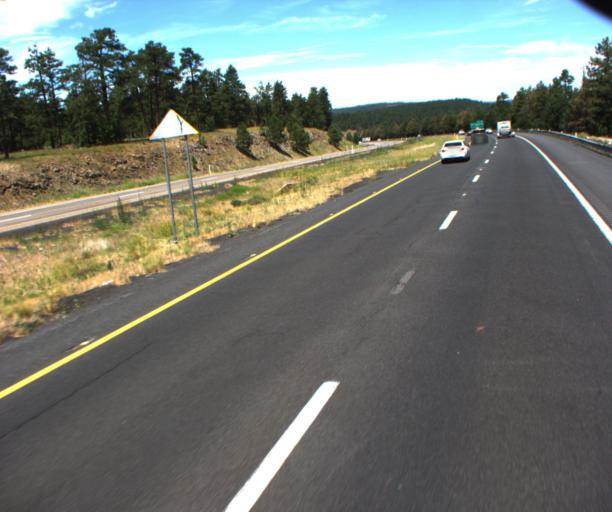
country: US
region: Arizona
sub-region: Coconino County
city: Sedona
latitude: 34.8618
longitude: -111.6166
